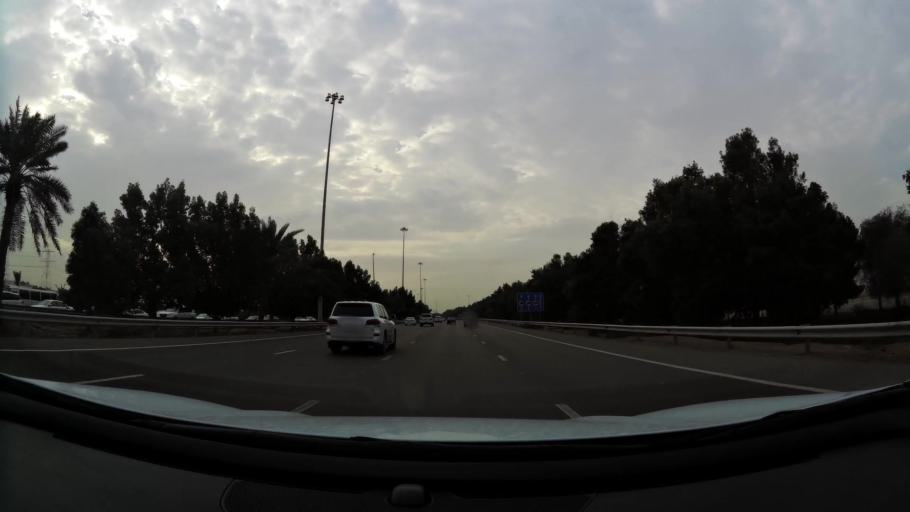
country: AE
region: Abu Dhabi
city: Abu Dhabi
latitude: 24.3511
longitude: 54.5696
